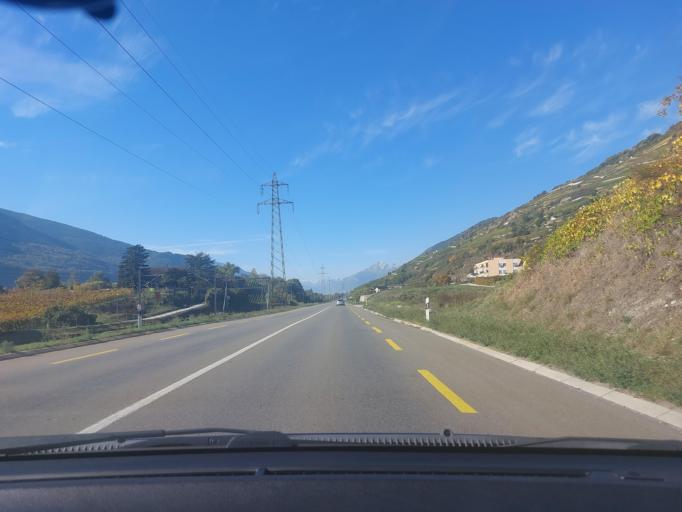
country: CH
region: Valais
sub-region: Sierre District
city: Chalais
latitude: 46.2785
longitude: 7.5048
